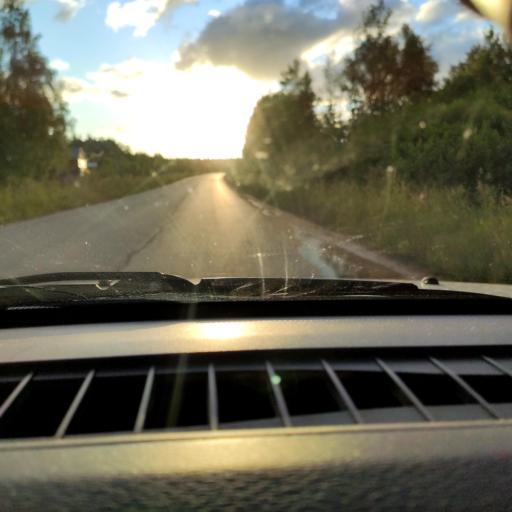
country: RU
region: Perm
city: Polazna
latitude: 58.2030
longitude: 56.4716
